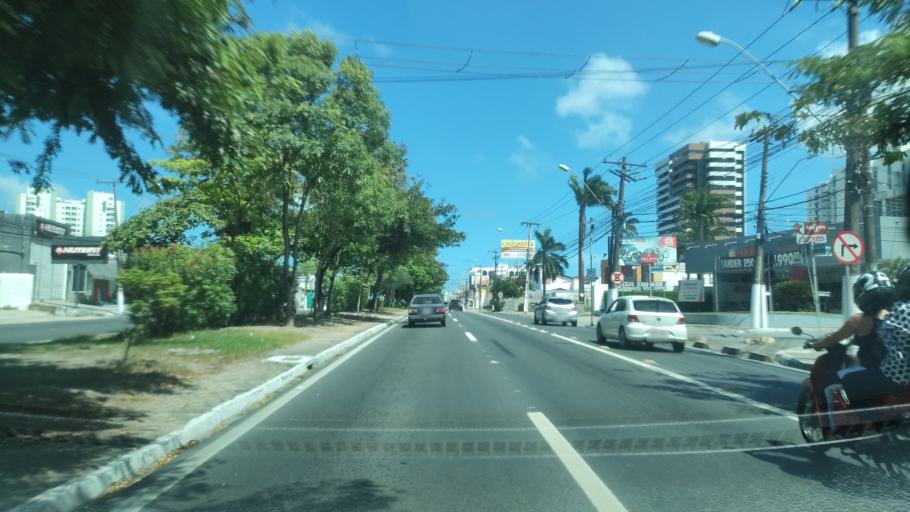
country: BR
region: Alagoas
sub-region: Maceio
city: Maceio
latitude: -9.6408
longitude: -35.7354
